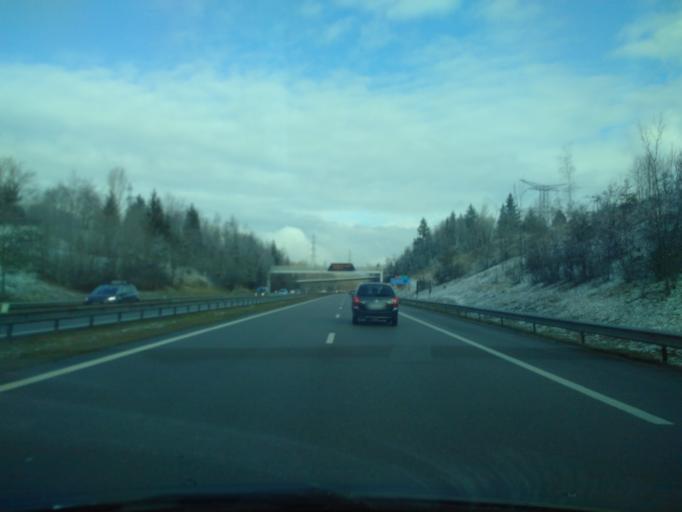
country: FR
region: Rhone-Alpes
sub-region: Departement de la Haute-Savoie
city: Chavanod
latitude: 45.8541
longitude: 6.0566
